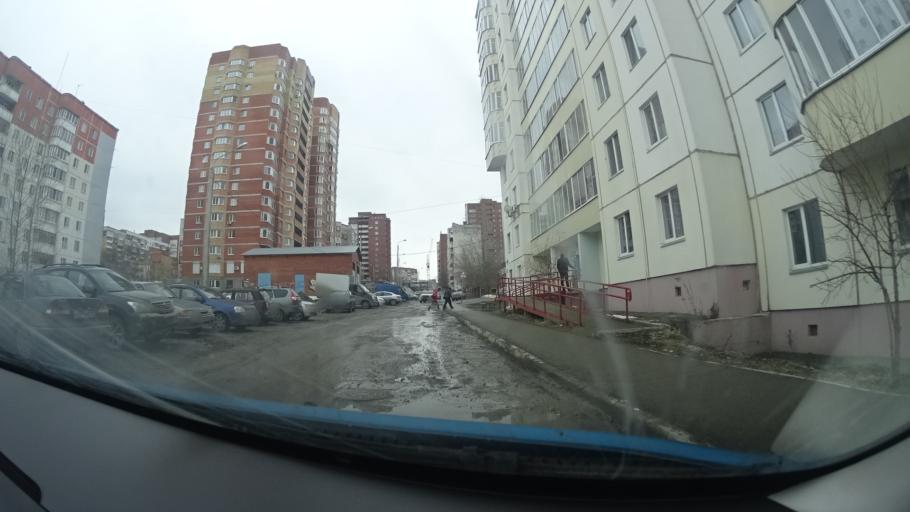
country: RU
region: Perm
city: Perm
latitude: 58.0104
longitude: 56.3034
